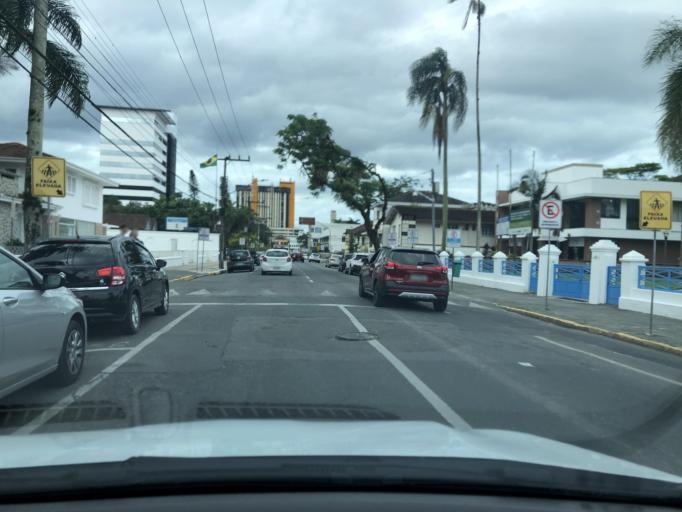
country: BR
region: Santa Catarina
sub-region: Joinville
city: Joinville
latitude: -26.3037
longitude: -48.8437
